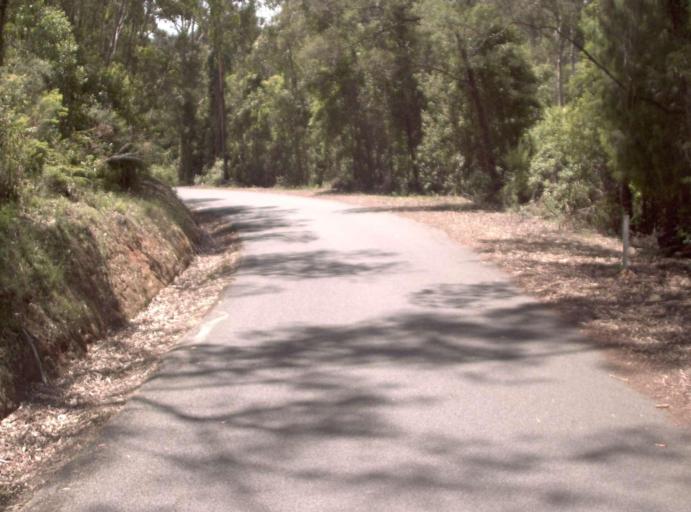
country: AU
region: New South Wales
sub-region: Bombala
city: Bombala
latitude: -37.4953
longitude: 148.9253
